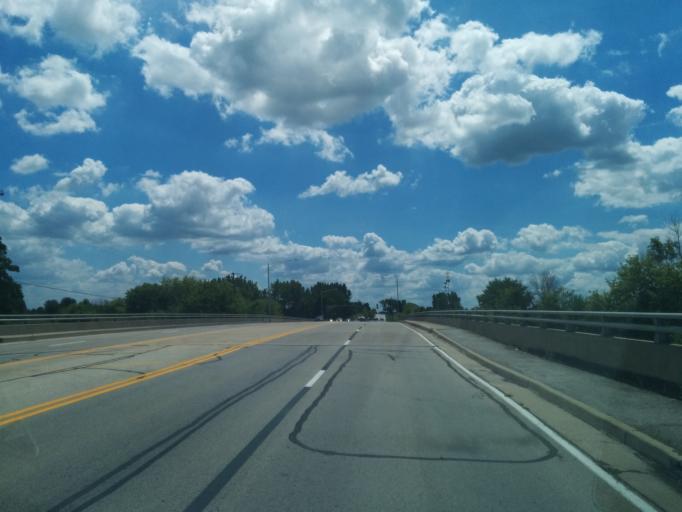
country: US
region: Illinois
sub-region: Will County
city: Plainfield
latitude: 41.6911
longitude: -88.1664
